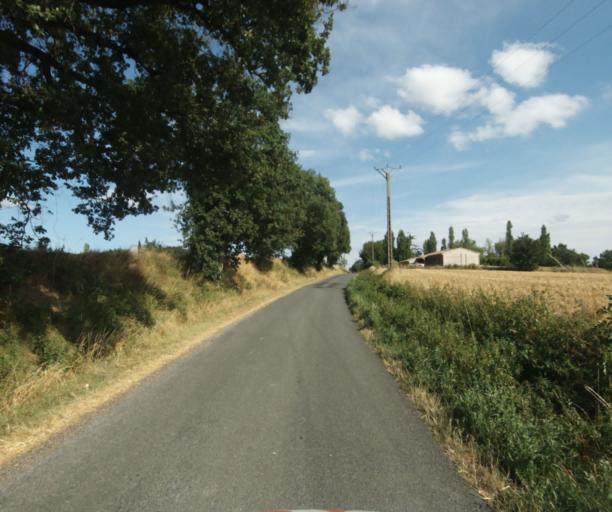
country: FR
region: Midi-Pyrenees
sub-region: Departement du Tarn
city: Puylaurens
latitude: 43.5284
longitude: 1.9772
